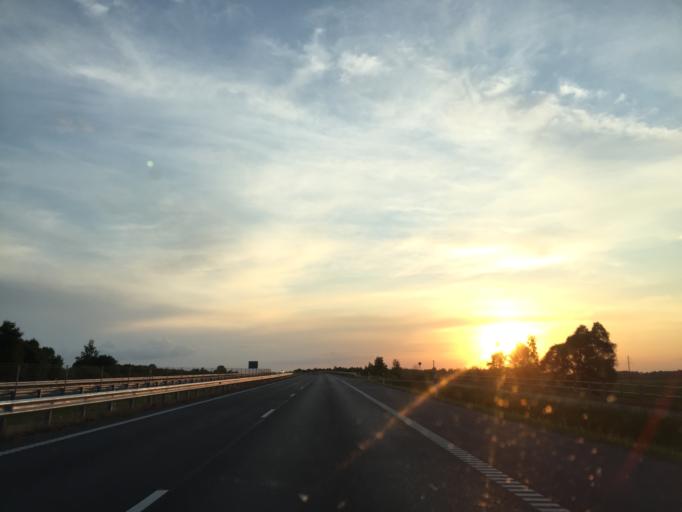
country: LT
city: Kursenai
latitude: 55.9873
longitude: 23.0809
